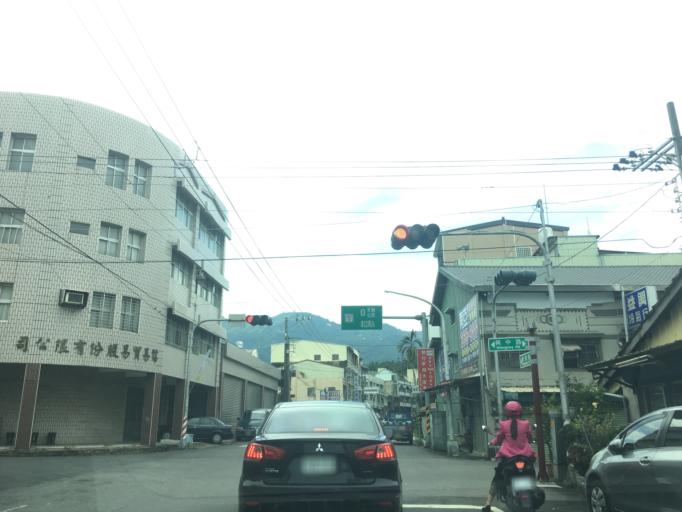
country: TW
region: Taiwan
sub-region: Yunlin
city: Douliu
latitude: 23.5837
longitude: 120.5597
